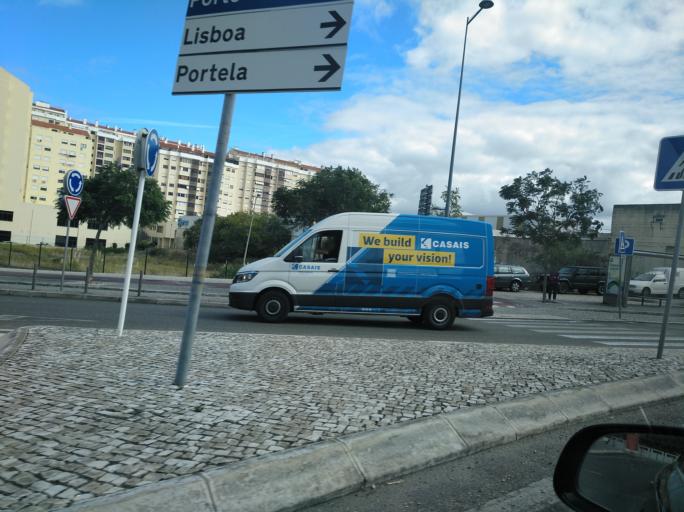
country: PT
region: Lisbon
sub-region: Loures
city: Sacavem
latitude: 38.7903
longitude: -9.1101
